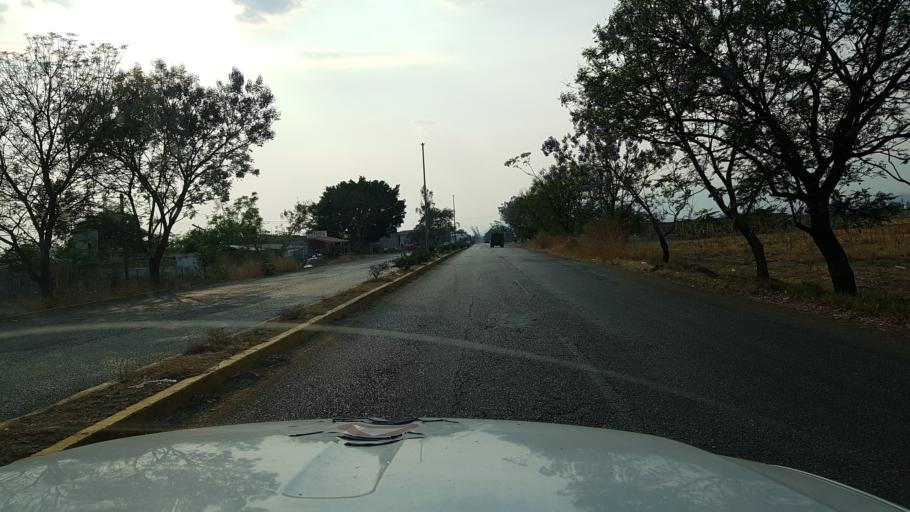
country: MX
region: Morelos
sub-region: Atlatlahucan
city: Colonia San Francisco
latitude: 18.8910
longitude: -98.8935
